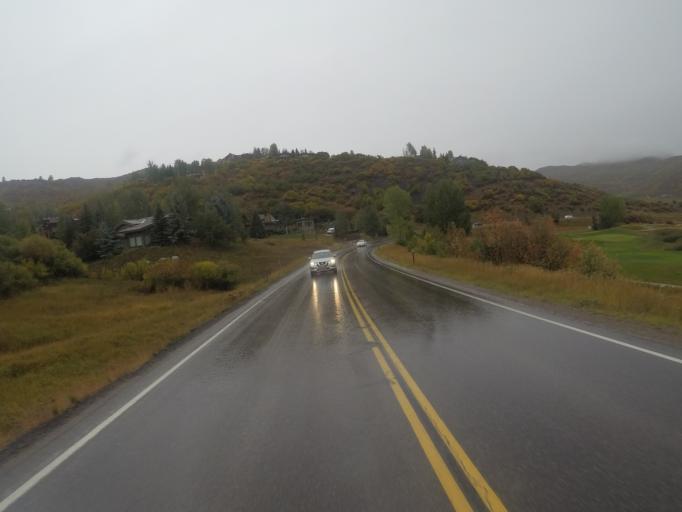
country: US
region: Colorado
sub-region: Pitkin County
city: Snowmass Village
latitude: 39.2205
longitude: -106.9320
